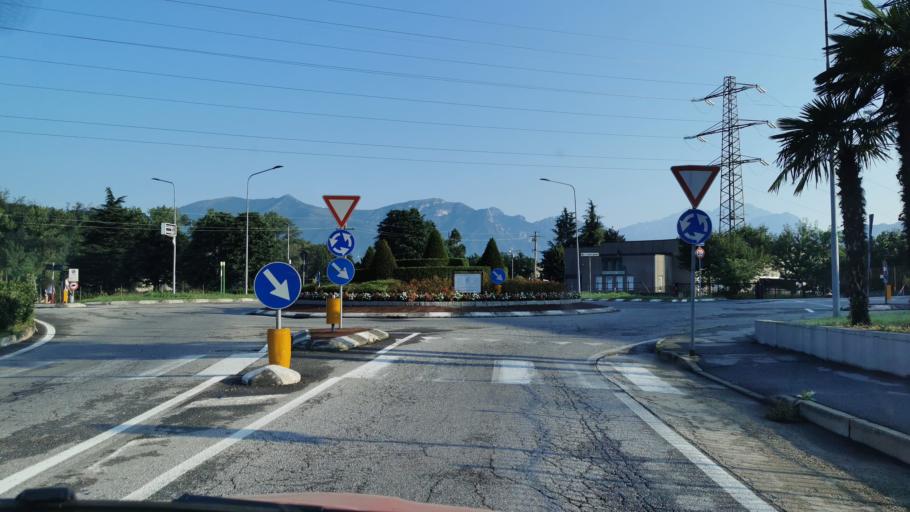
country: IT
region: Lombardy
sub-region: Provincia di Lecco
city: Dolzago
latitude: 45.7710
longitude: 9.3388
